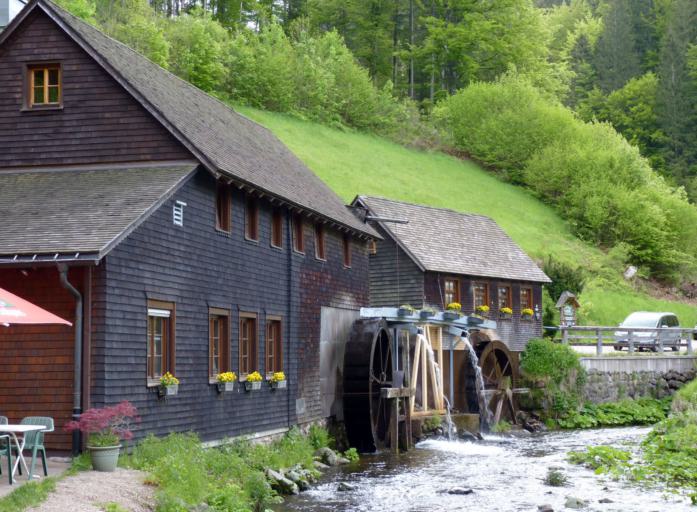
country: DE
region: Baden-Wuerttemberg
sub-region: Freiburg Region
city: Gutenbach
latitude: 48.0093
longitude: 8.1398
